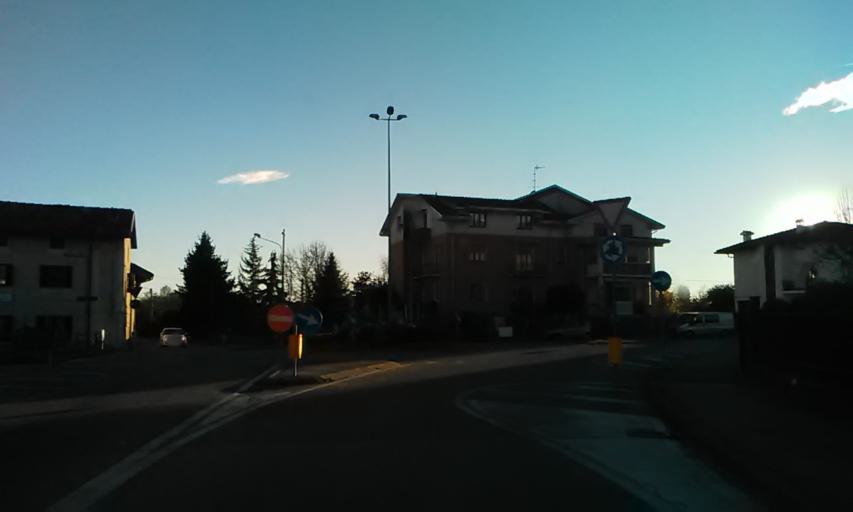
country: IT
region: Piedmont
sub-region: Provincia di Biella
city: Valdengo
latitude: 45.5689
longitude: 8.1362
